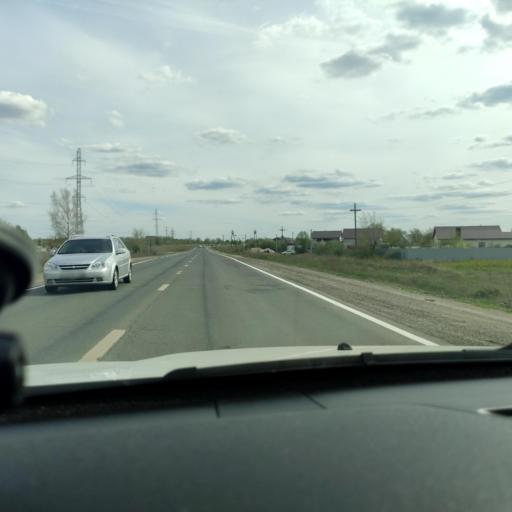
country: RU
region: Samara
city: Kinel'
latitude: 53.1974
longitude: 50.6375
